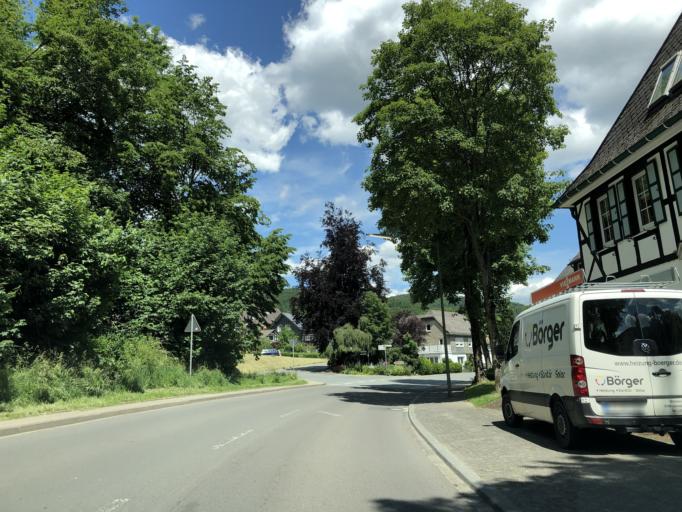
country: DE
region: North Rhine-Westphalia
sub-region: Regierungsbezirk Arnsberg
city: Kirchhundem
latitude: 51.1206
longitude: 8.1694
